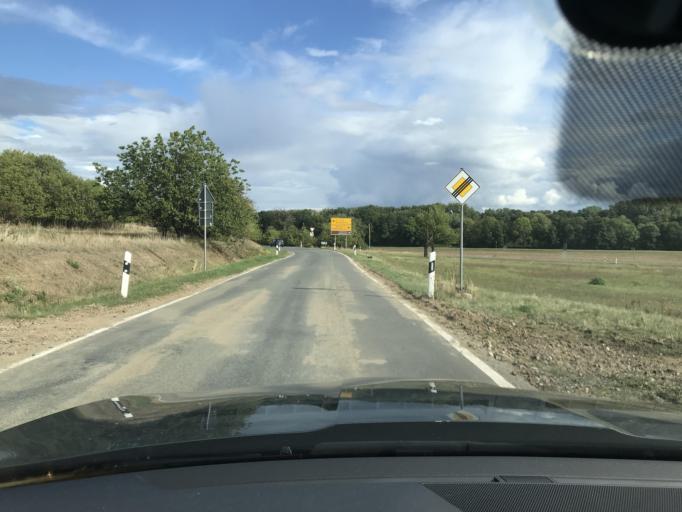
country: DE
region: Saxony-Anhalt
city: Weddersleben
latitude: 51.7751
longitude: 11.1026
